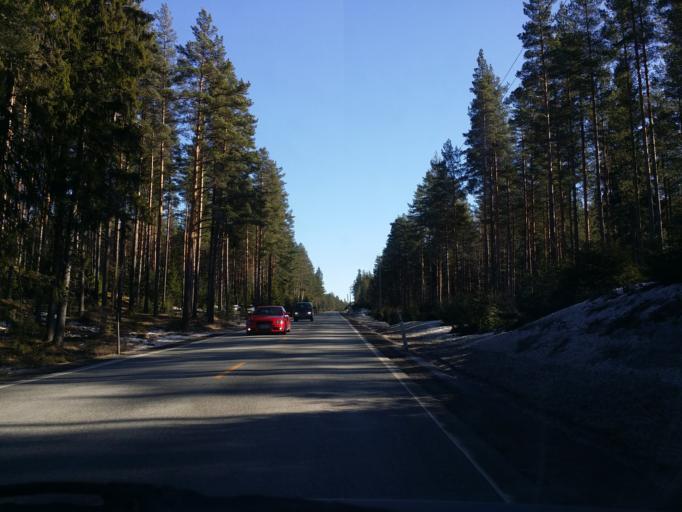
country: NO
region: Buskerud
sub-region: Ringerike
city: Honefoss
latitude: 60.3191
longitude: 10.1406
